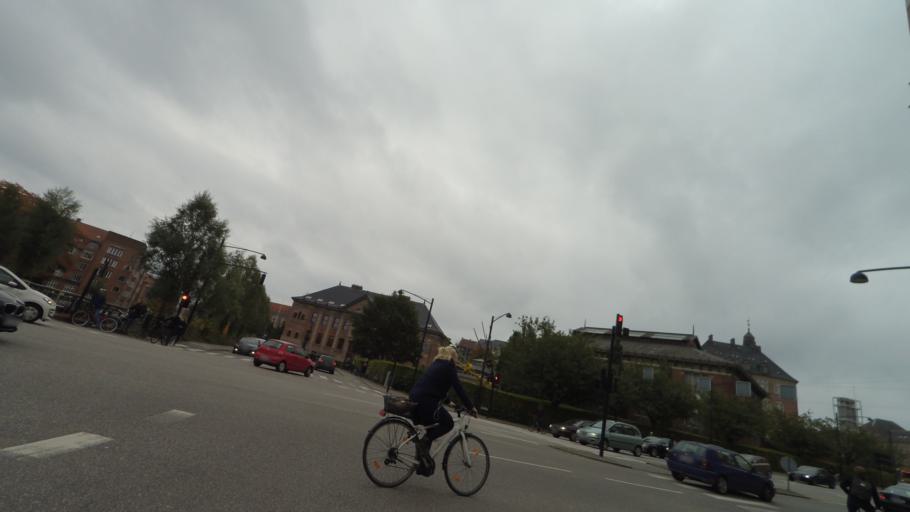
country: DK
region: Central Jutland
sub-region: Arhus Kommune
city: Arhus
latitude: 56.1552
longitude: 10.1993
